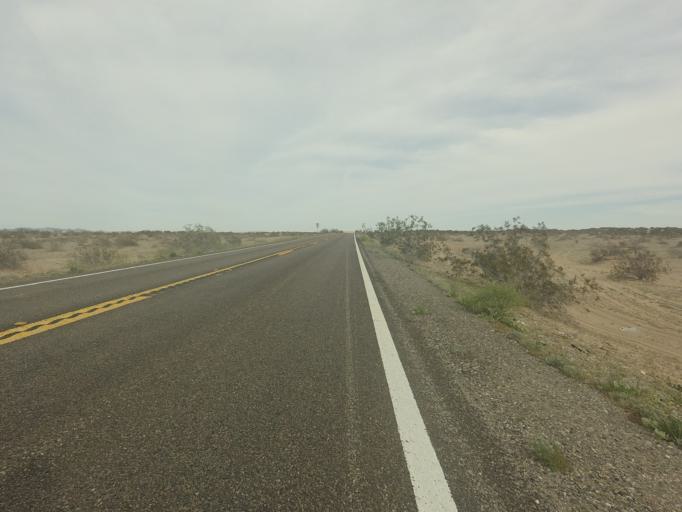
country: US
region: California
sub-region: Imperial County
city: Holtville
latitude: 32.9705
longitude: -115.2320
